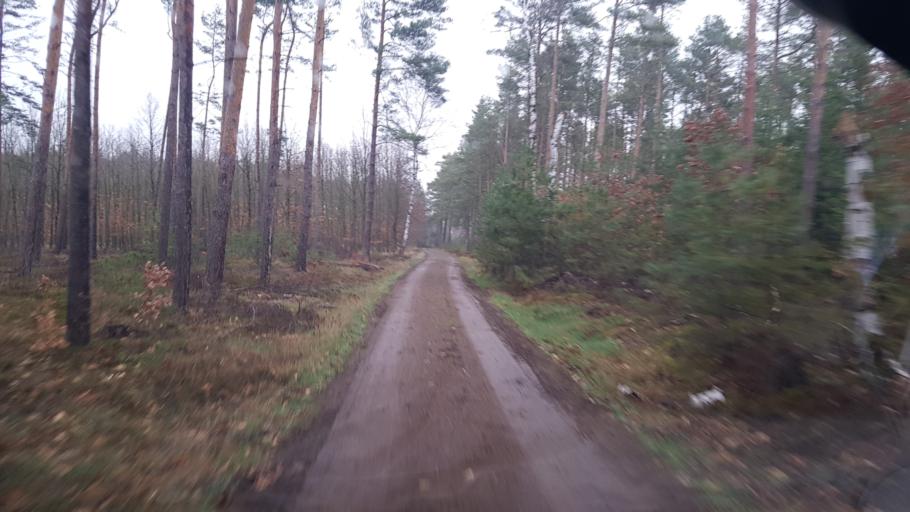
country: DE
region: Brandenburg
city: Muhlberg
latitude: 51.4906
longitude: 13.2992
